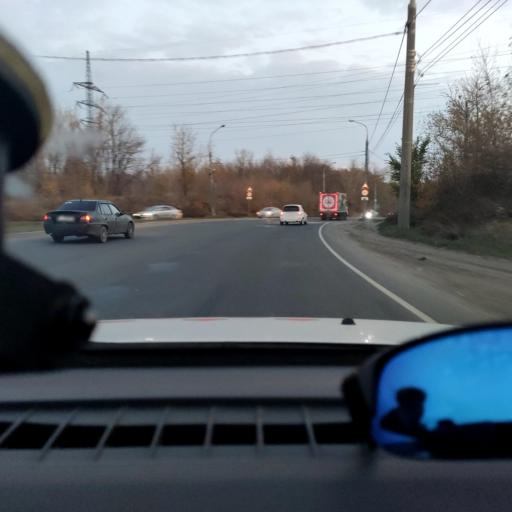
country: RU
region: Samara
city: Samara
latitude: 53.1272
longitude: 50.1713
